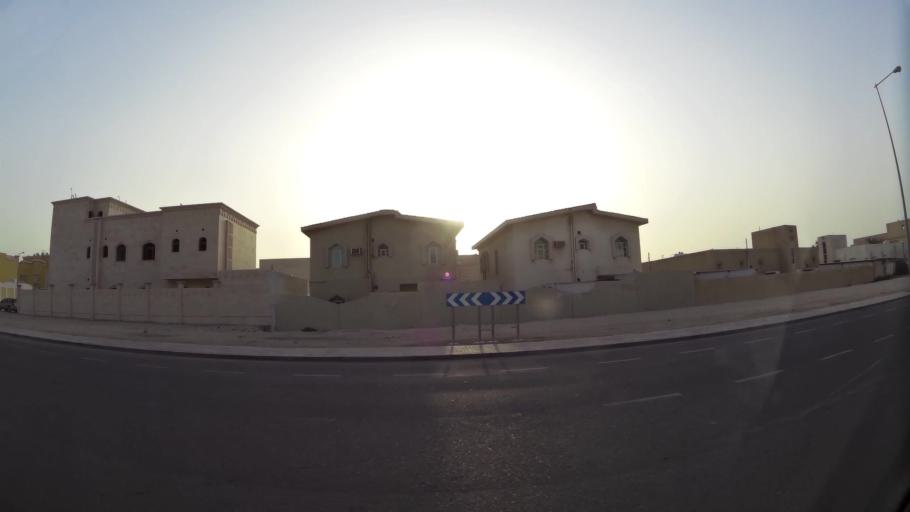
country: QA
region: Baladiyat ar Rayyan
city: Ar Rayyan
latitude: 25.2472
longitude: 51.4437
